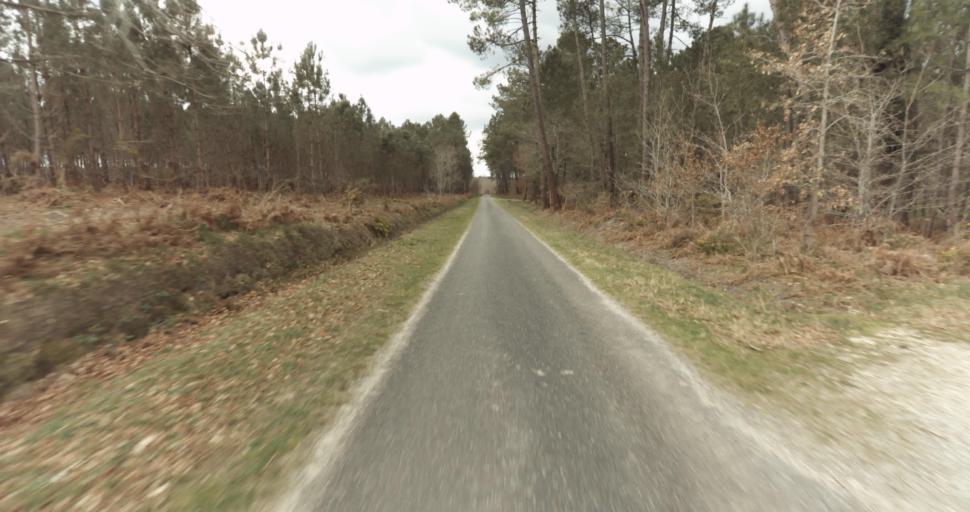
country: FR
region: Aquitaine
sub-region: Departement des Landes
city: Sarbazan
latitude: 44.0165
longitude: -0.3018
